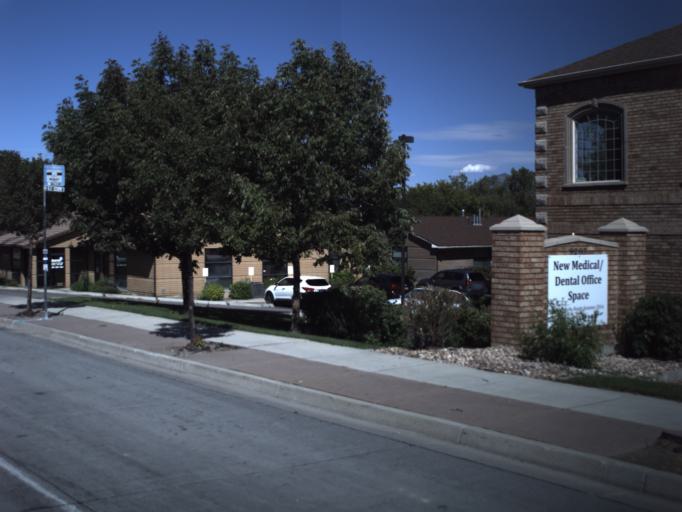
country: US
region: Utah
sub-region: Salt Lake County
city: South Jordan Heights
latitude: 40.5823
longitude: -111.9386
